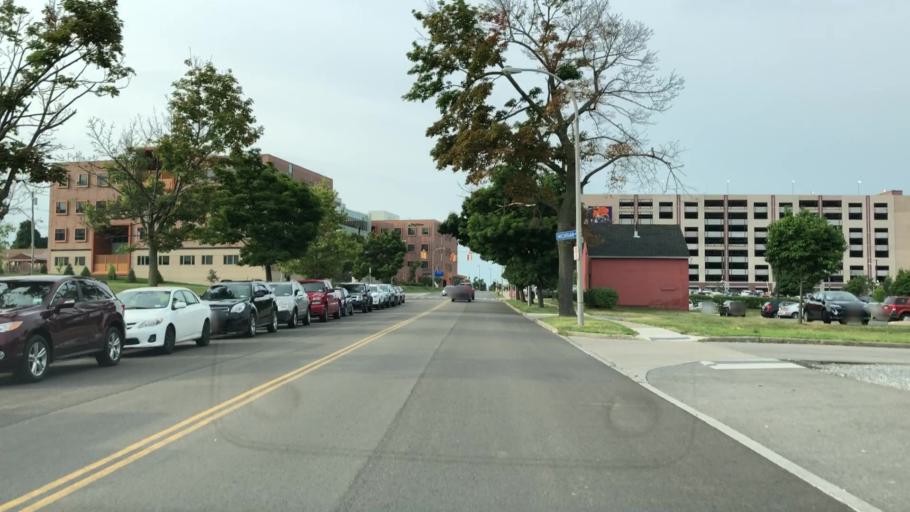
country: US
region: New York
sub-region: Erie County
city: Buffalo
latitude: 42.9031
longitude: -78.8626
